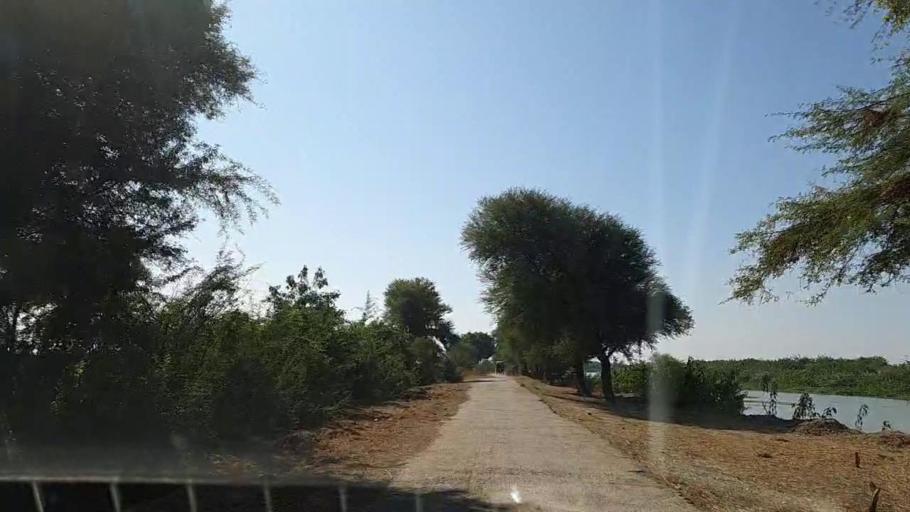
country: PK
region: Sindh
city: Chuhar Jamali
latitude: 24.5835
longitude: 68.0476
